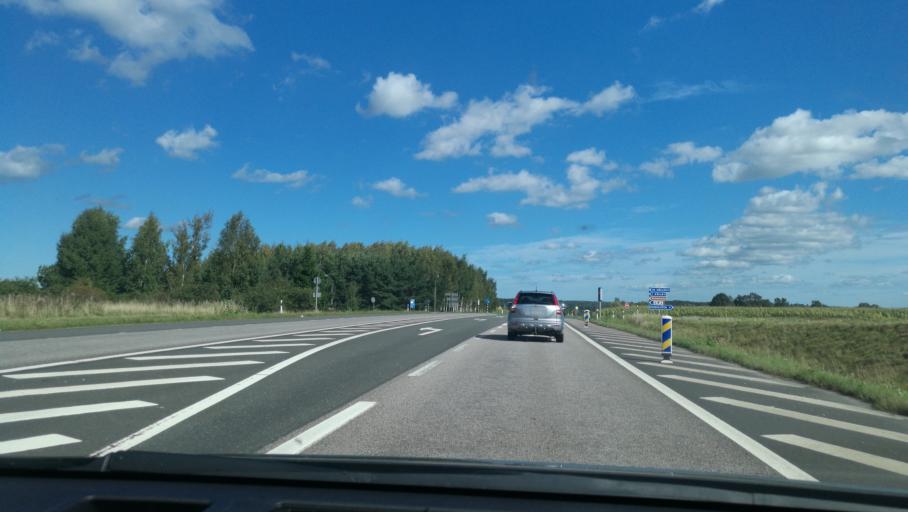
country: SE
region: Vaestra Goetaland
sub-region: Gotene Kommun
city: Kallby
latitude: 58.5037
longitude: 13.3099
